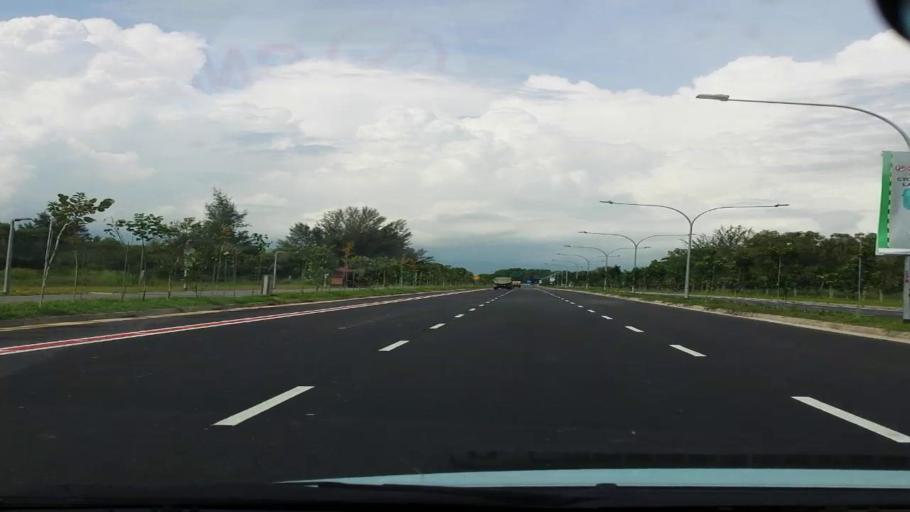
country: SG
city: Singapore
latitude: 1.3240
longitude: 104.0182
